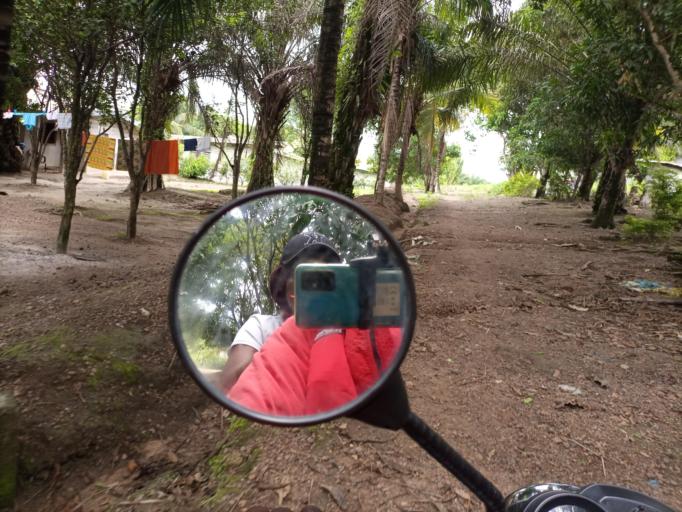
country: SL
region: Southern Province
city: Bo
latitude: 7.9408
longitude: -11.7458
